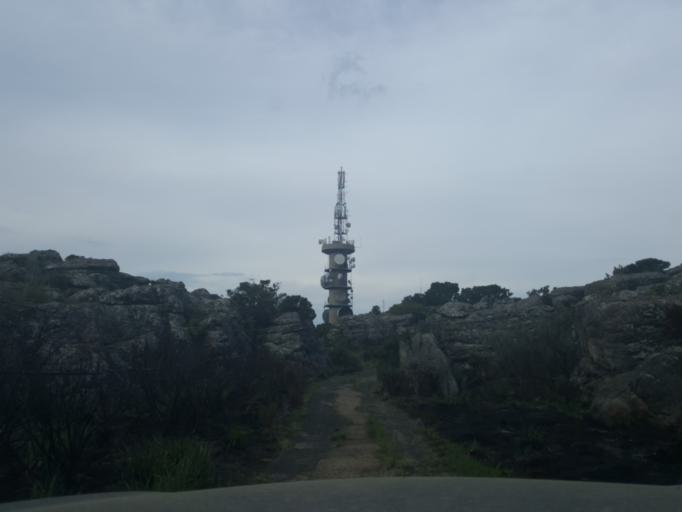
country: ZA
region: Limpopo
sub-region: Mopani District Municipality
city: Hoedspruit
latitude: -24.5411
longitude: 30.8697
